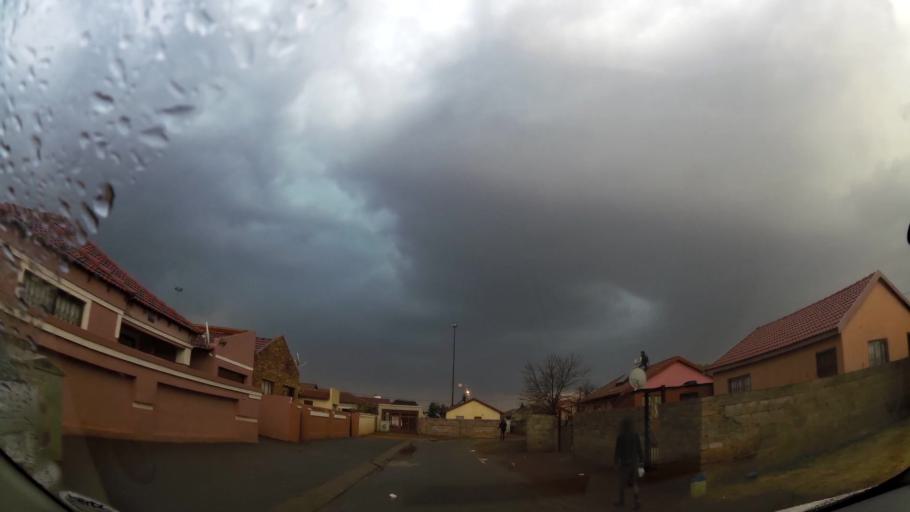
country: ZA
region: Gauteng
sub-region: Ekurhuleni Metropolitan Municipality
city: Germiston
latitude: -26.3627
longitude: 28.1296
